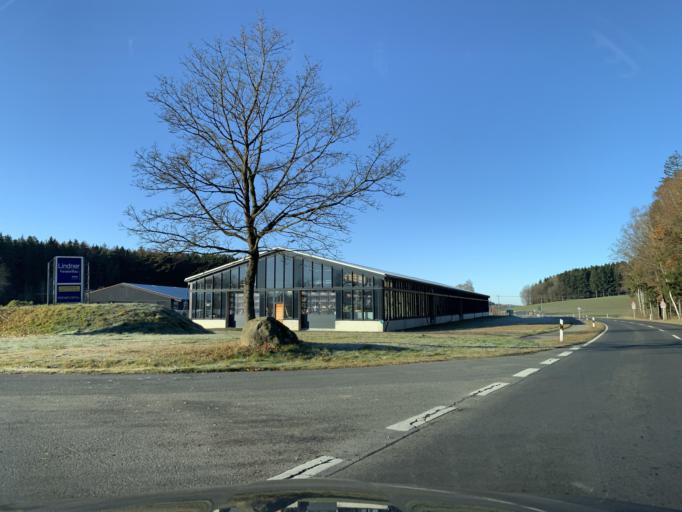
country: DE
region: Bavaria
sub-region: Upper Palatinate
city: Oberviechtach
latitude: 49.4685
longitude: 12.4570
